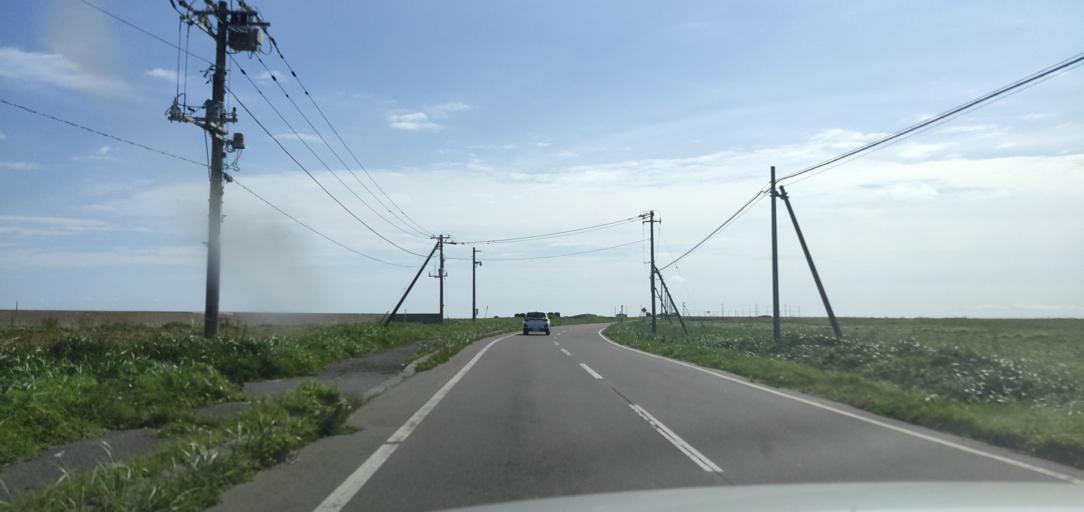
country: JP
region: Hokkaido
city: Shibetsu
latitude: 43.6276
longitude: 145.1995
